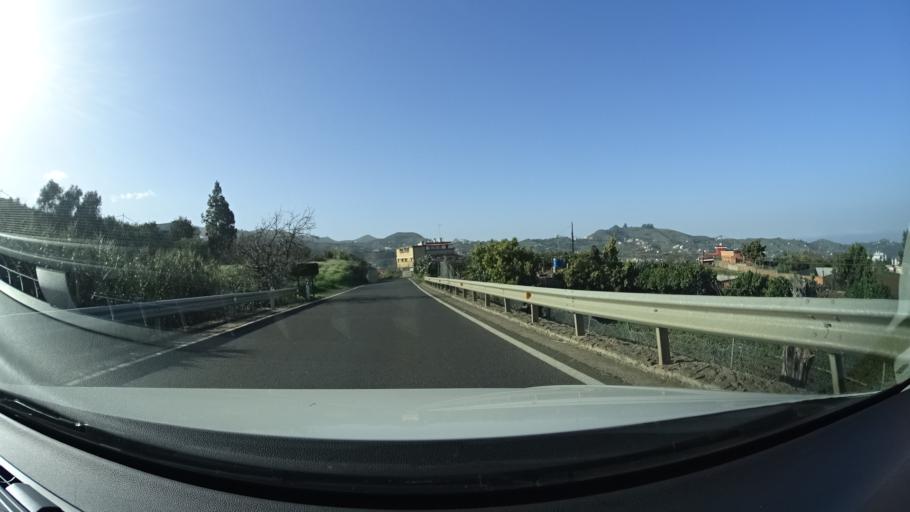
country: ES
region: Canary Islands
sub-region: Provincia de Las Palmas
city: Vega de San Mateo
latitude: 28.0145
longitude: -15.5363
